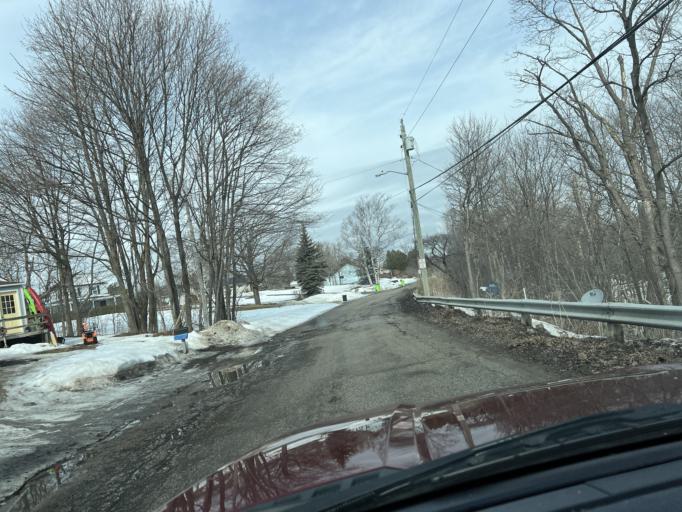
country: US
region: Michigan
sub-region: Mackinac County
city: Saint Ignace
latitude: 45.8694
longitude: -84.7331
